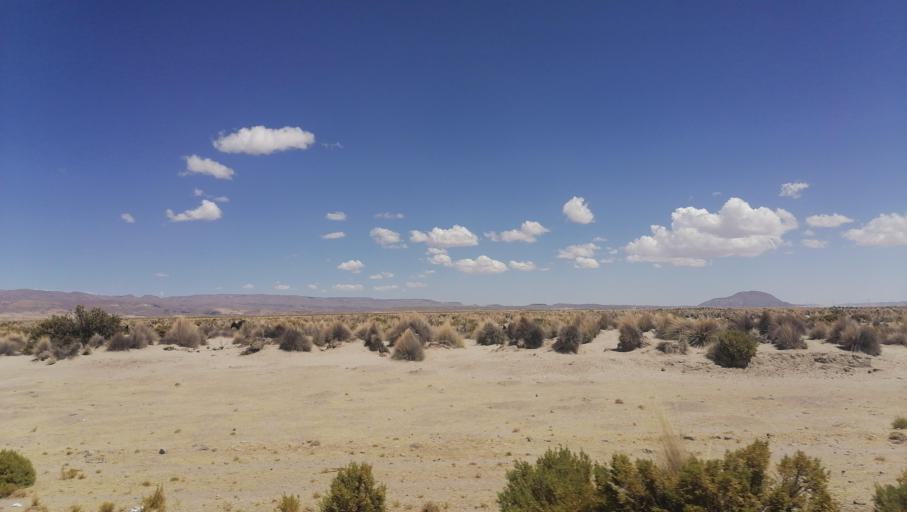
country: BO
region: Oruro
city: Challapata
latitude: -19.1712
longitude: -66.7926
